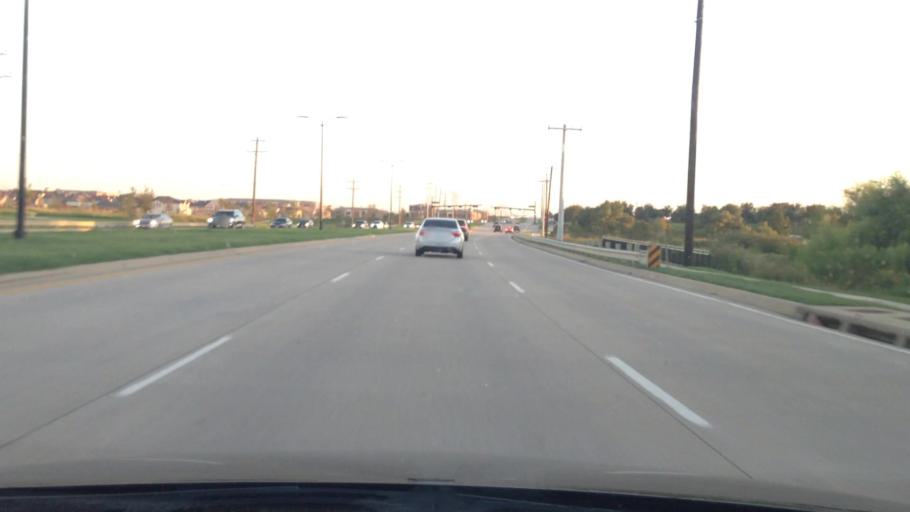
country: US
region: Texas
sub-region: Denton County
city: The Colony
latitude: 33.1397
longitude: -96.8908
